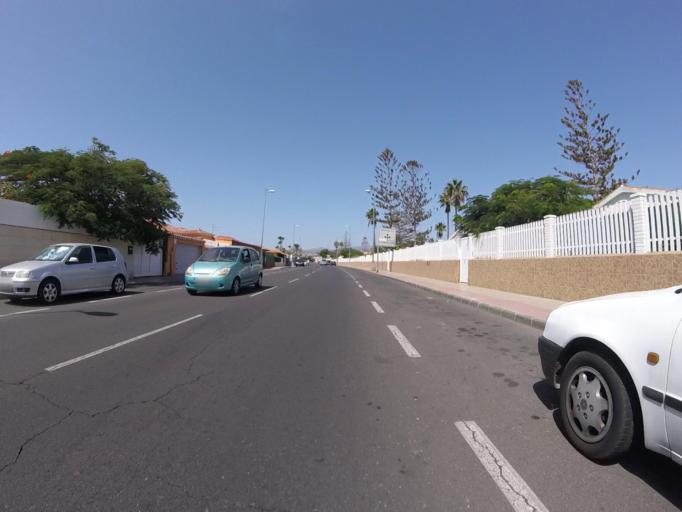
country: ES
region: Canary Islands
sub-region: Provincia de Las Palmas
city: Playa del Ingles
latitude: 27.7577
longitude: -15.5820
